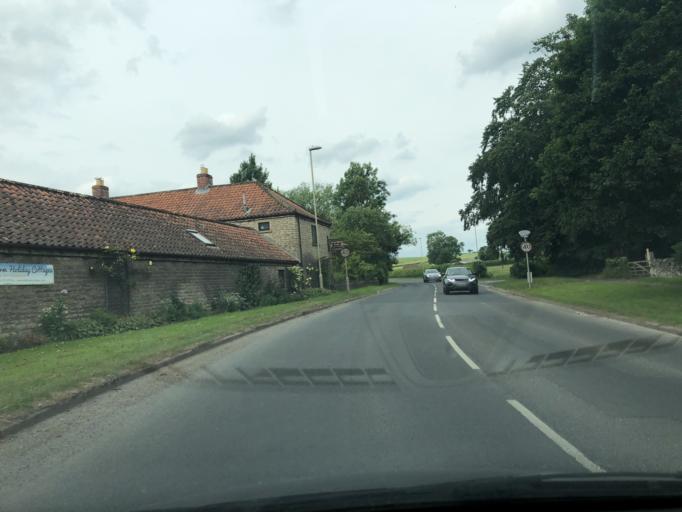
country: GB
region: England
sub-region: North Yorkshire
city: Pickering
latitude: 54.2512
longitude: -0.7941
